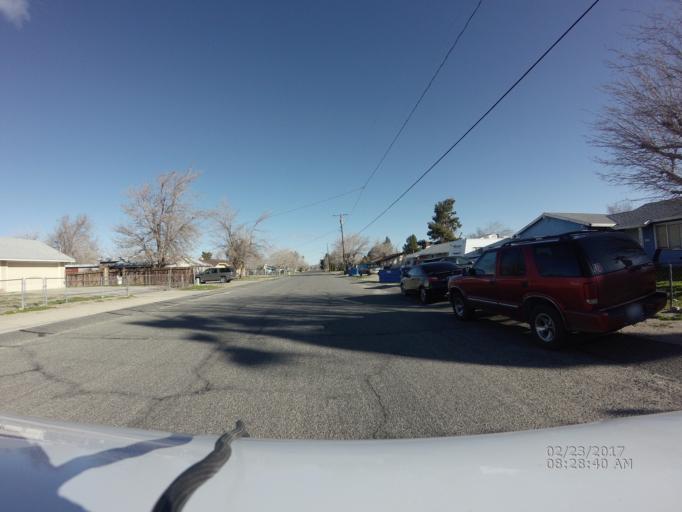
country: US
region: California
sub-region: Los Angeles County
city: Lake Los Angeles
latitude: 34.6117
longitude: -117.8313
